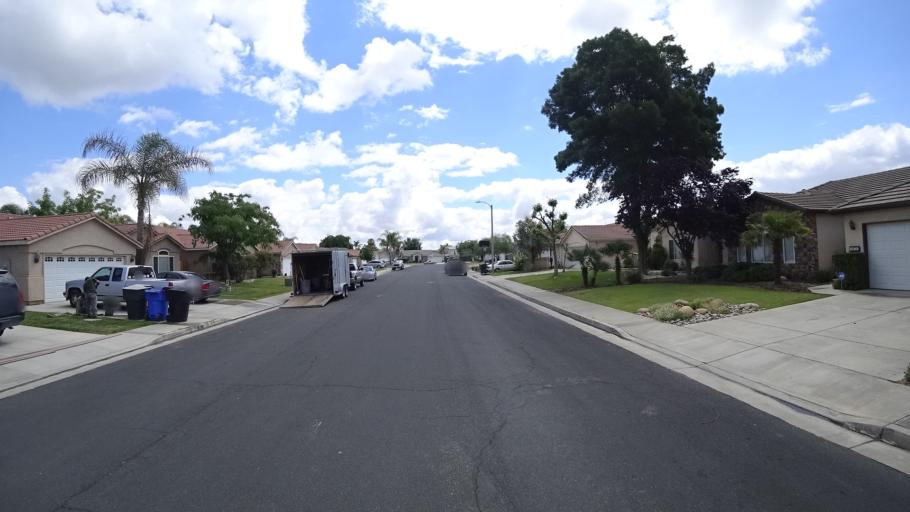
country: US
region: California
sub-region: Kings County
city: Lucerne
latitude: 36.3625
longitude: -119.6617
